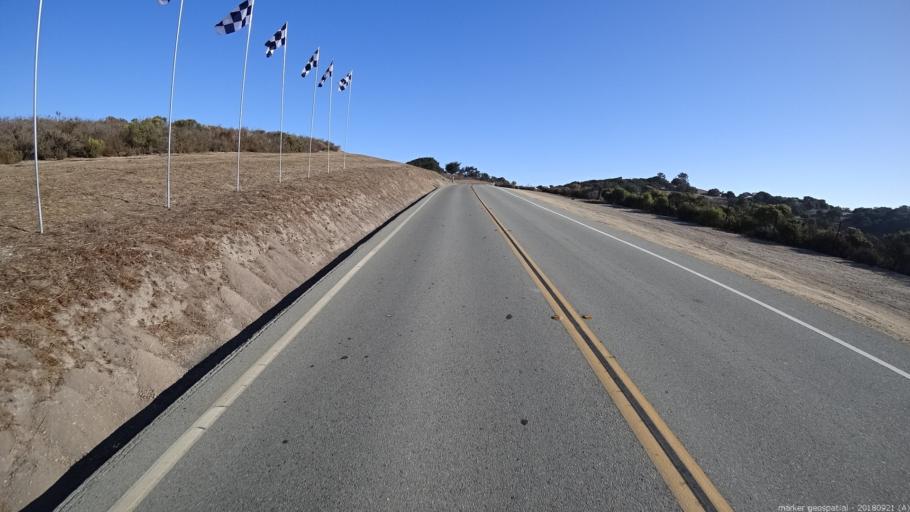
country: US
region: California
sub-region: Monterey County
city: Carmel Valley Village
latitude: 36.5751
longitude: -121.7611
